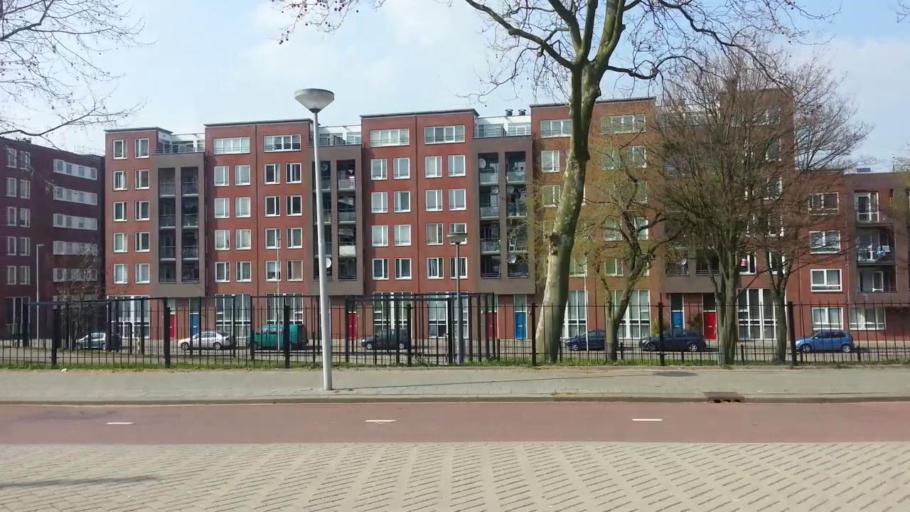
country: NL
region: South Holland
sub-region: Gemeente Rotterdam
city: Delfshaven
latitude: 51.9140
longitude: 4.4330
